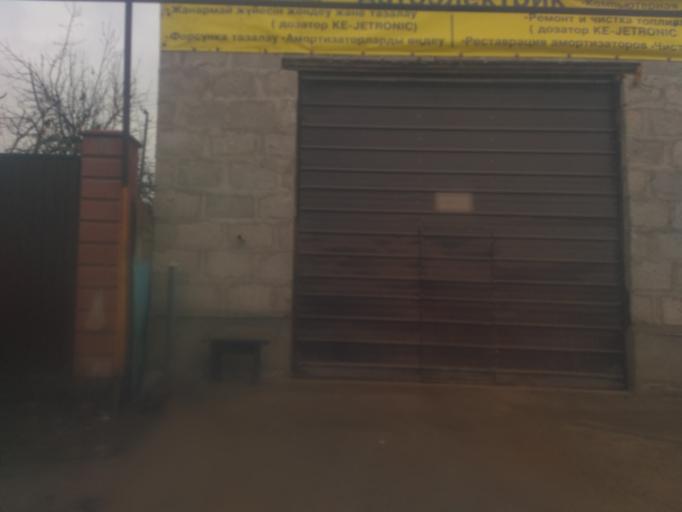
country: KZ
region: Almaty Oblysy
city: Burunday
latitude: 43.2184
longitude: 76.7599
